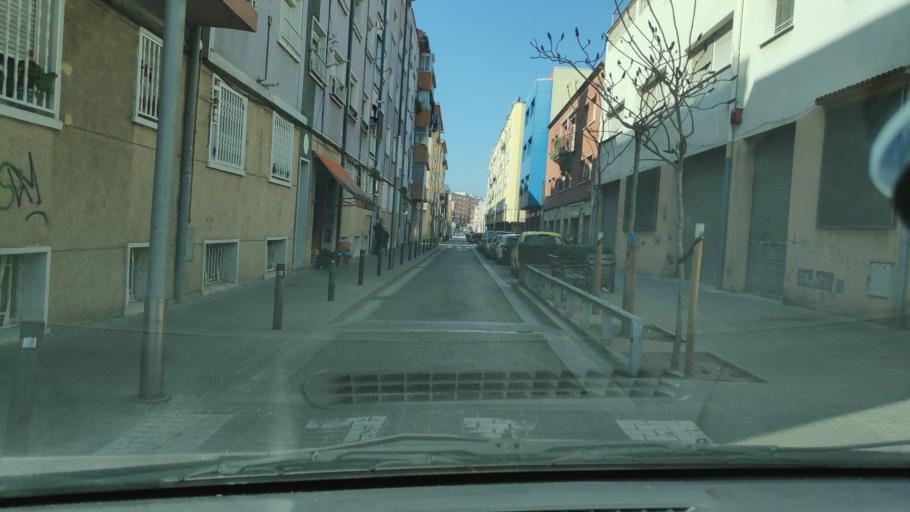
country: ES
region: Catalonia
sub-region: Provincia de Barcelona
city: Mollet del Valles
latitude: 41.5428
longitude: 2.2099
